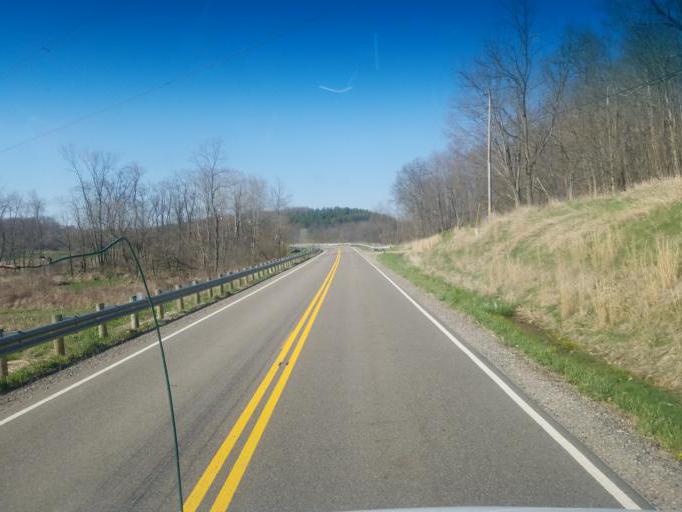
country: US
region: Ohio
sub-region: Muskingum County
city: Frazeysburg
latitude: 40.2243
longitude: -82.1661
